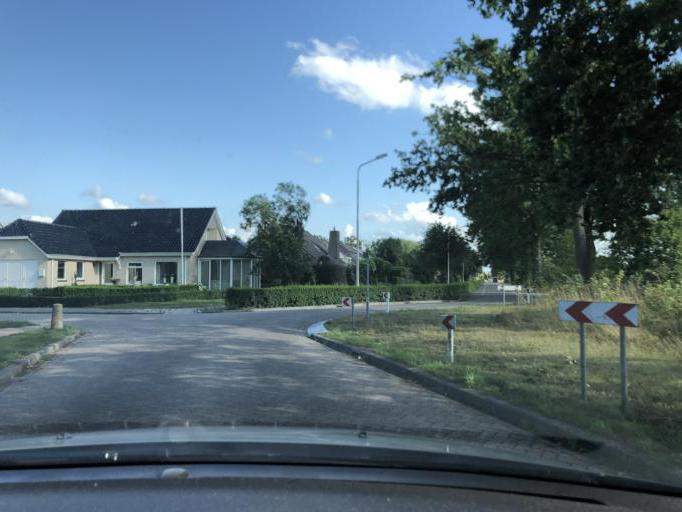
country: NL
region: Overijssel
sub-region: Gemeente Dalfsen
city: Dalfsen
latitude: 52.5861
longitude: 6.2743
